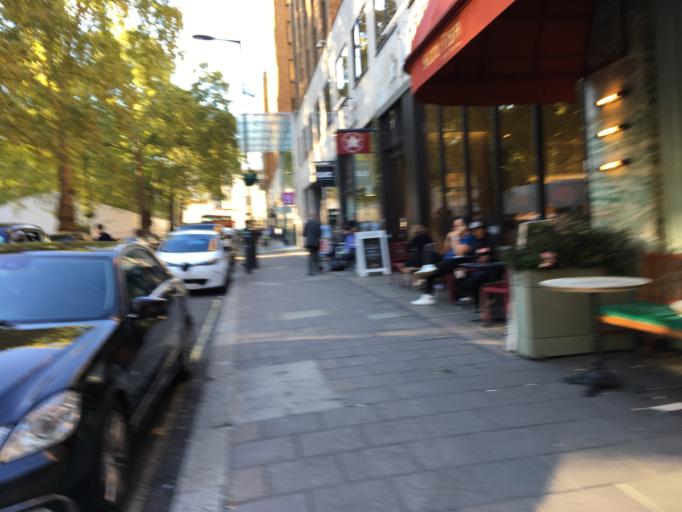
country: GB
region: England
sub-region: Greater London
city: London
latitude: 51.5094
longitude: -0.1446
